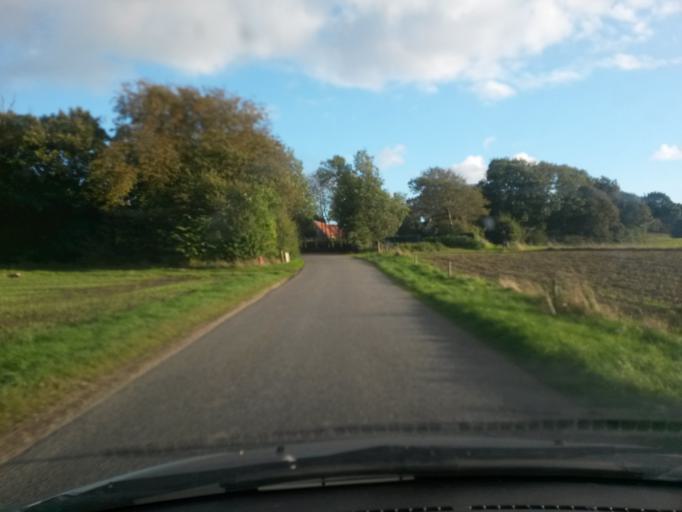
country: DK
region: Central Jutland
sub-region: Silkeborg Kommune
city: Kjellerup
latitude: 56.3299
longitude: 9.3731
